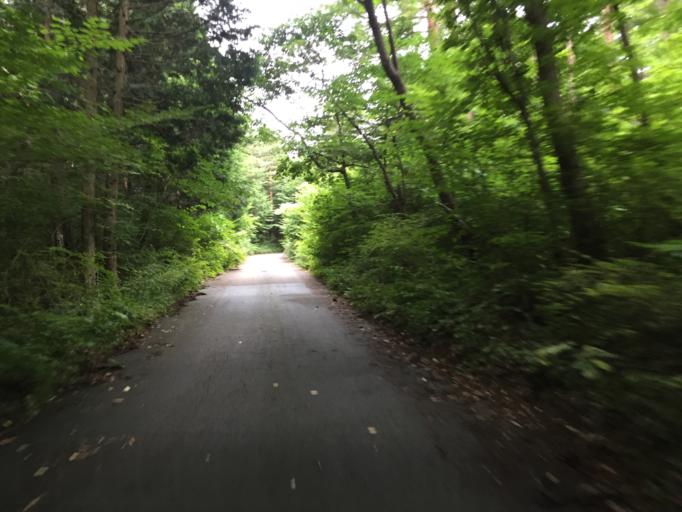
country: JP
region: Fukushima
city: Motomiya
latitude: 37.5669
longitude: 140.3143
